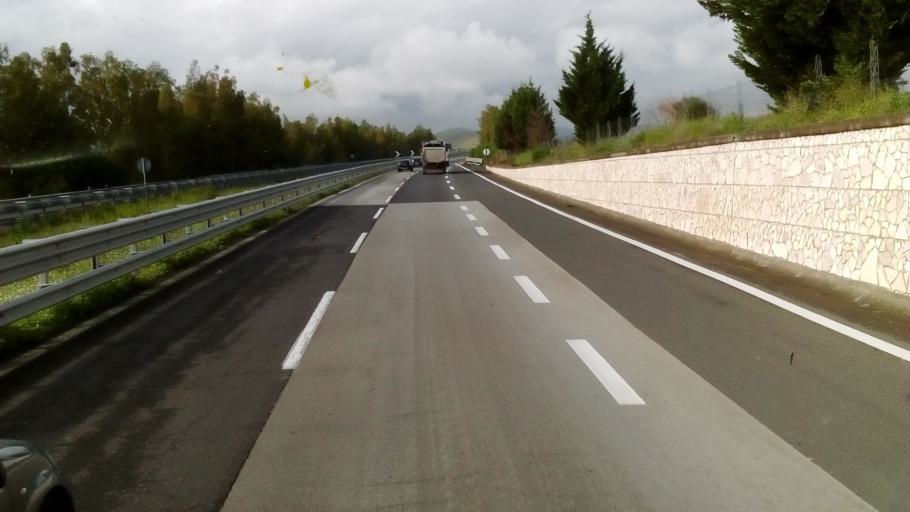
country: IT
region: Sicily
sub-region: Enna
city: Assoro
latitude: 37.5705
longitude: 14.4718
